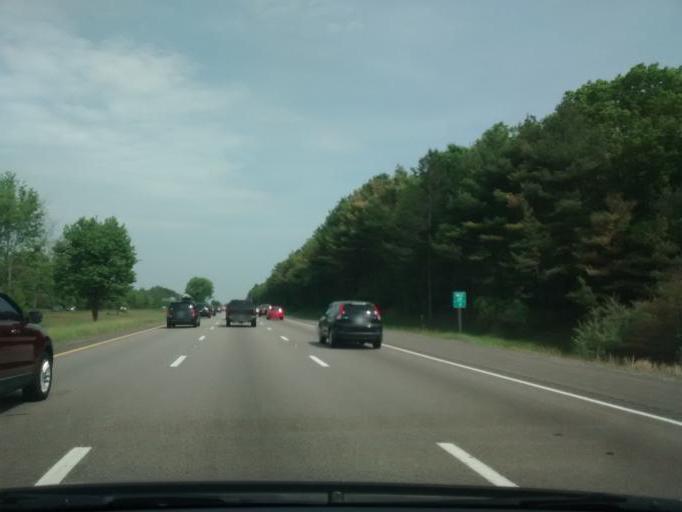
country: US
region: Massachusetts
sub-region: Bristol County
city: Mansfield Center
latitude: 41.9984
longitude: -71.2027
